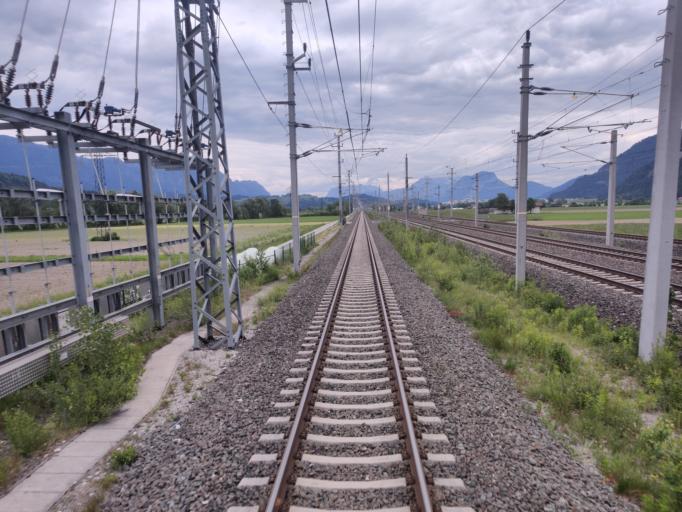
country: AT
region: Tyrol
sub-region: Politischer Bezirk Kufstein
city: Radfeld
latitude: 47.4579
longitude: 11.9418
